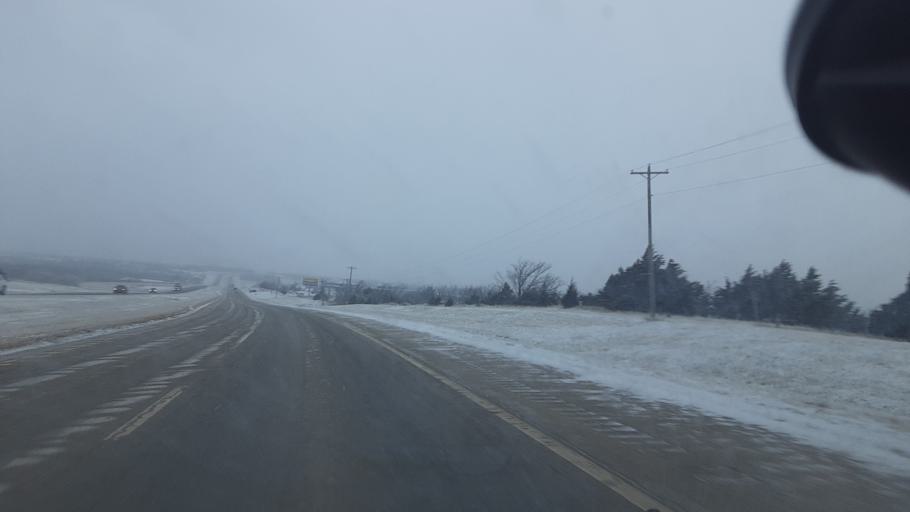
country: US
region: Oklahoma
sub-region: Logan County
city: Guthrie
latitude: 35.8982
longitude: -97.3559
